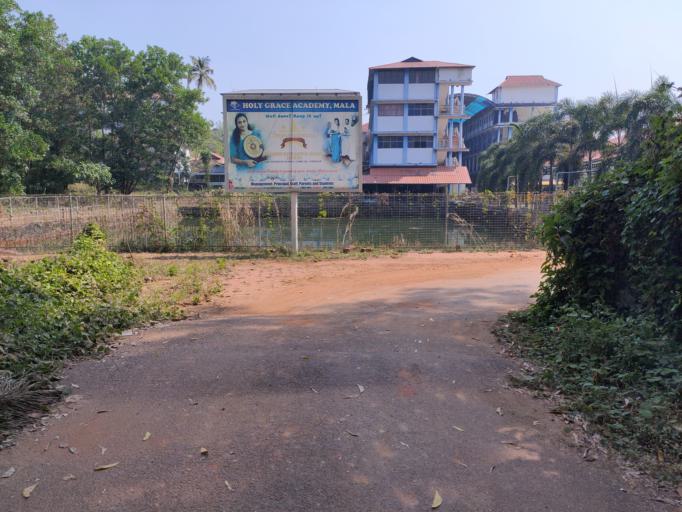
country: IN
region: Kerala
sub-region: Thrissur District
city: Kodungallur
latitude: 10.2334
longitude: 76.2778
